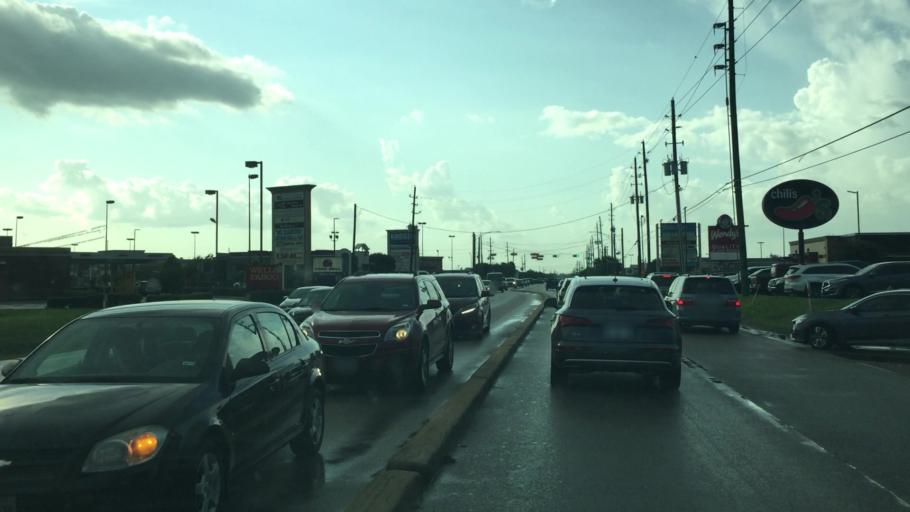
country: US
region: Texas
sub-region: Montgomery County
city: The Woodlands
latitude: 30.0745
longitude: -95.5138
